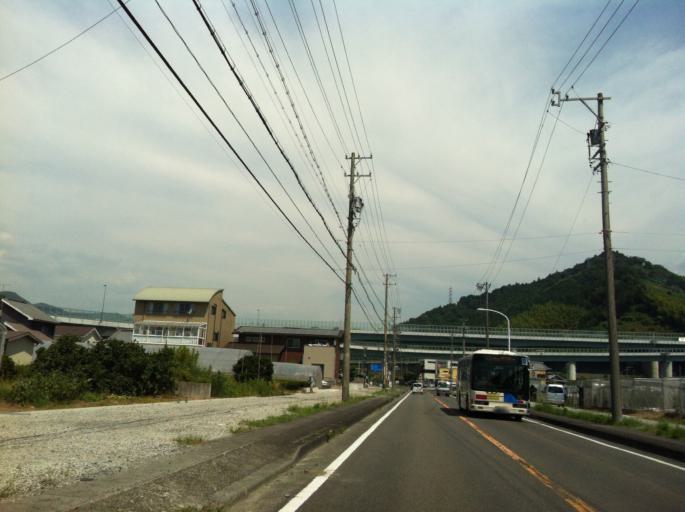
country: JP
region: Shizuoka
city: Shizuoka-shi
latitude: 35.0385
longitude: 138.3798
